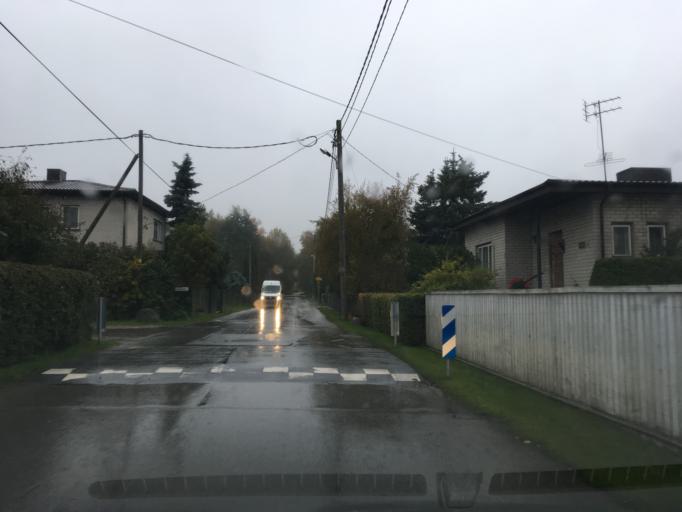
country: EE
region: Harju
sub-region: Tallinna linn
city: Kose
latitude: 59.4556
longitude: 24.8510
